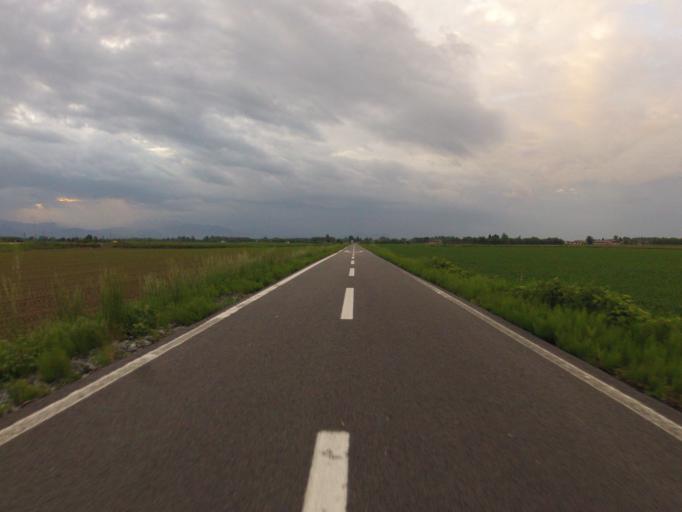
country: IT
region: Piedmont
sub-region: Provincia di Torino
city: Villafranca Piemonte
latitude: 44.7979
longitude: 7.5055
